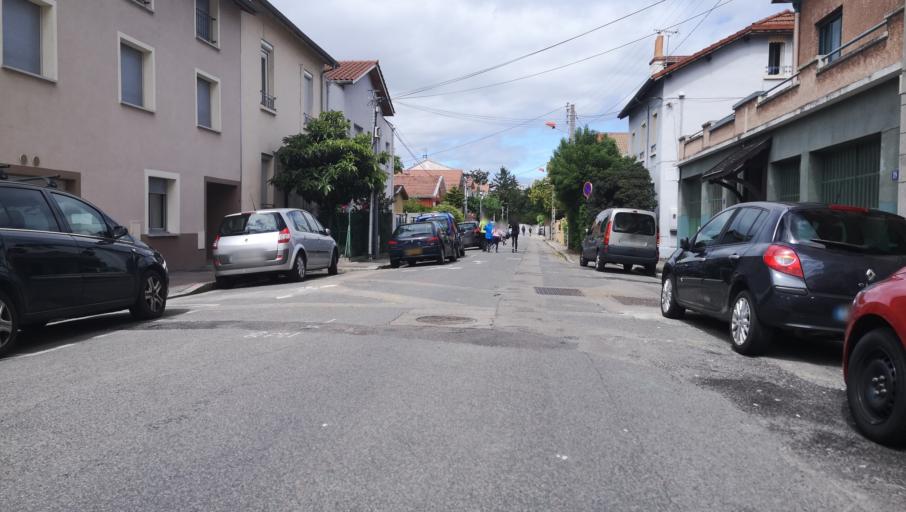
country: FR
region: Rhone-Alpes
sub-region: Departement du Rhone
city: Villeurbanne
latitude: 45.7732
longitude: 4.8755
